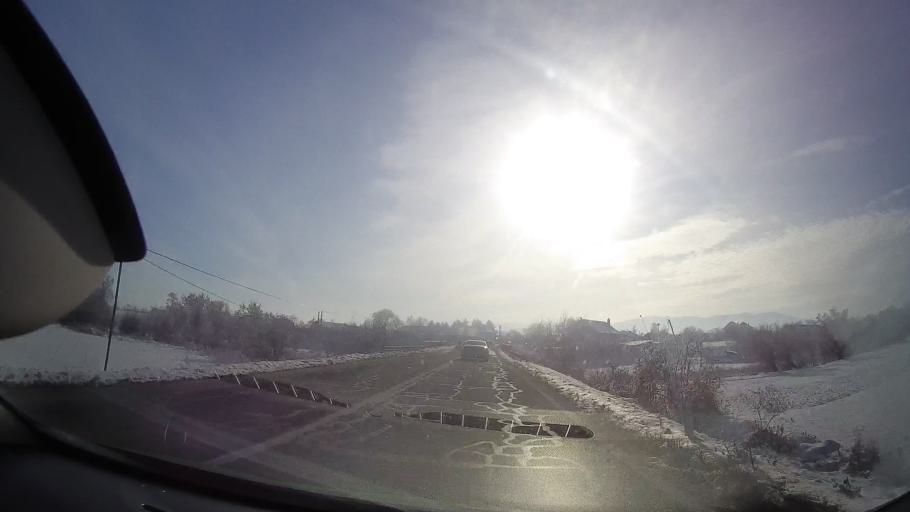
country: RO
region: Neamt
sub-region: Comuna Dobreni
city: Dobreni
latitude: 47.0038
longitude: 26.4238
